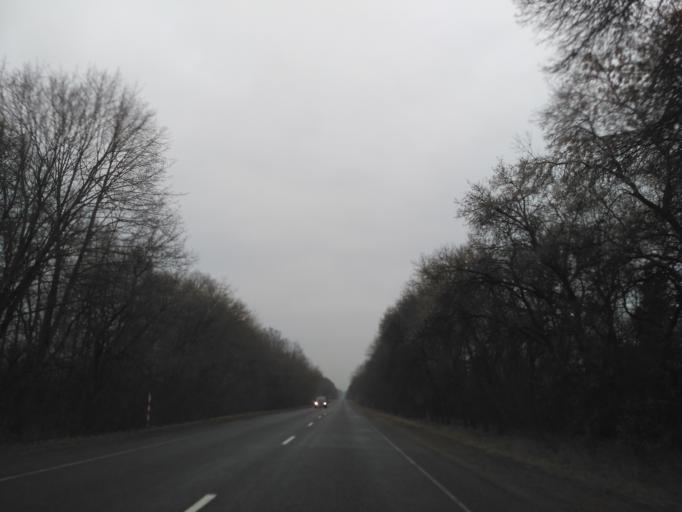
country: BY
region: Minsk
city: Snow
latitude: 53.2588
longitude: 26.3054
